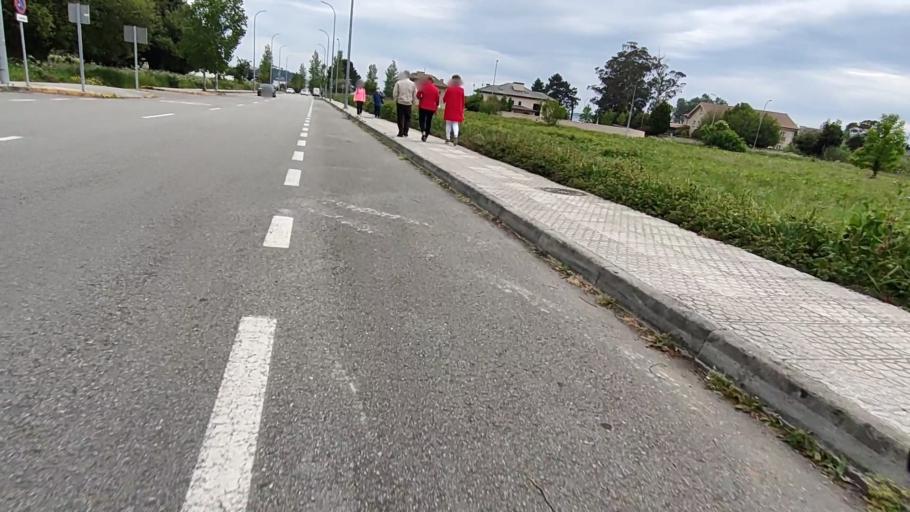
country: ES
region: Galicia
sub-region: Provincia da Coruna
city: Boiro
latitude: 42.6429
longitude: -8.8868
